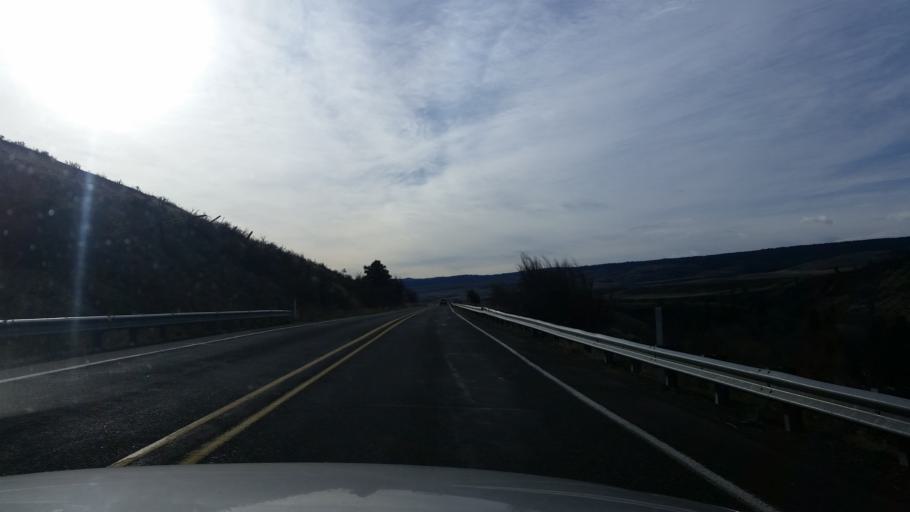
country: US
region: Washington
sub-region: Kittitas County
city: Ellensburg
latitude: 47.1140
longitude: -120.7159
